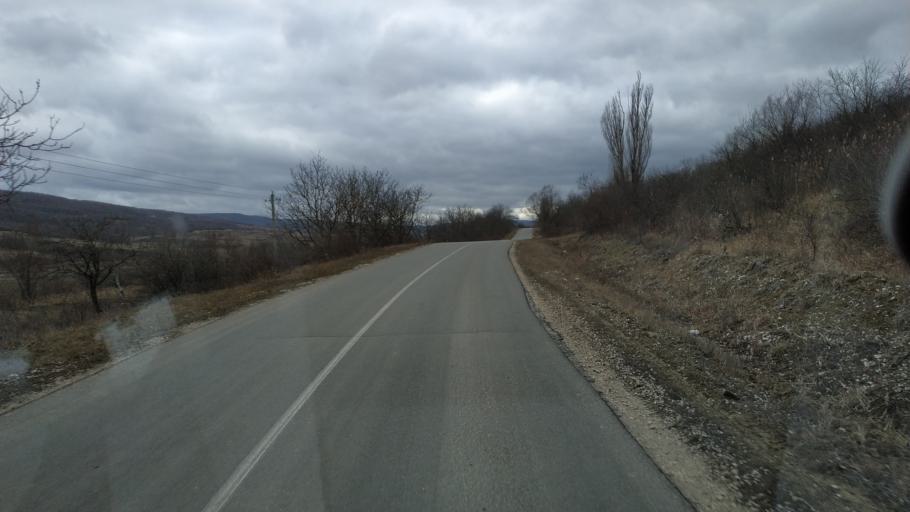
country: MD
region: Calarasi
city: Calarasi
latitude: 47.2392
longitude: 28.1785
